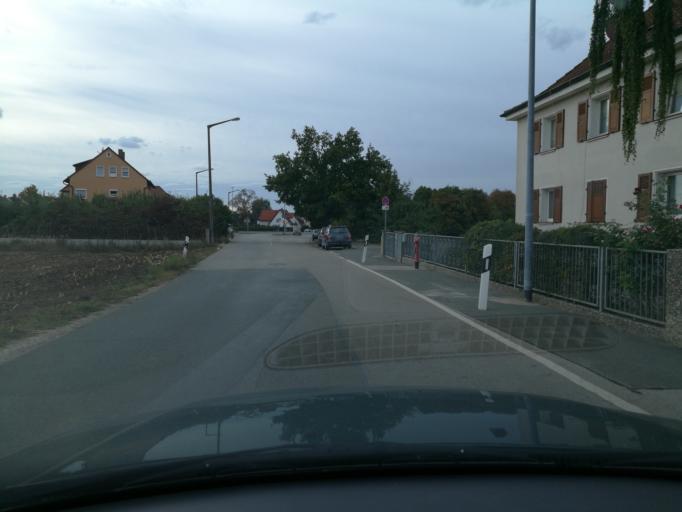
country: DE
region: Bavaria
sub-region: Regierungsbezirk Mittelfranken
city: Wetzendorf
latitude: 49.5135
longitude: 11.0359
